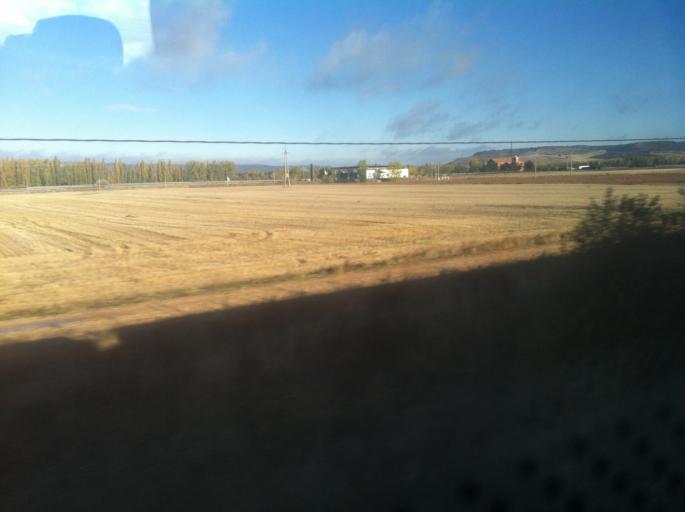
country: ES
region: Castille and Leon
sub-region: Provincia de Palencia
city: Cordovilla la Real
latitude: 42.0440
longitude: -4.2551
